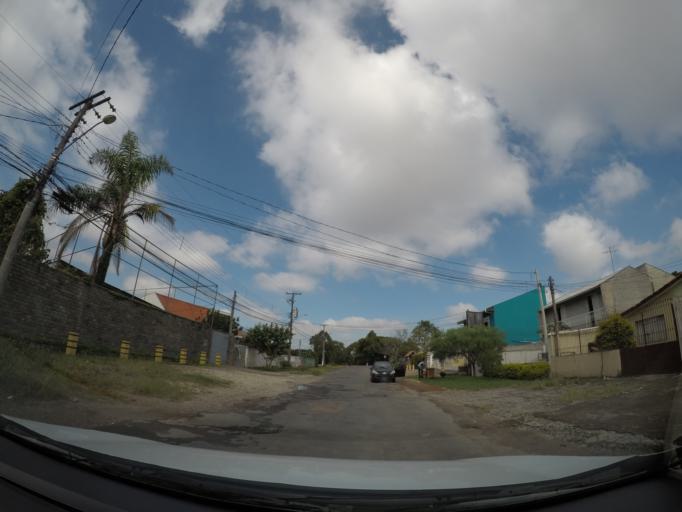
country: BR
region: Parana
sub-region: Sao Jose Dos Pinhais
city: Sao Jose dos Pinhais
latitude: -25.4910
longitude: -49.2211
